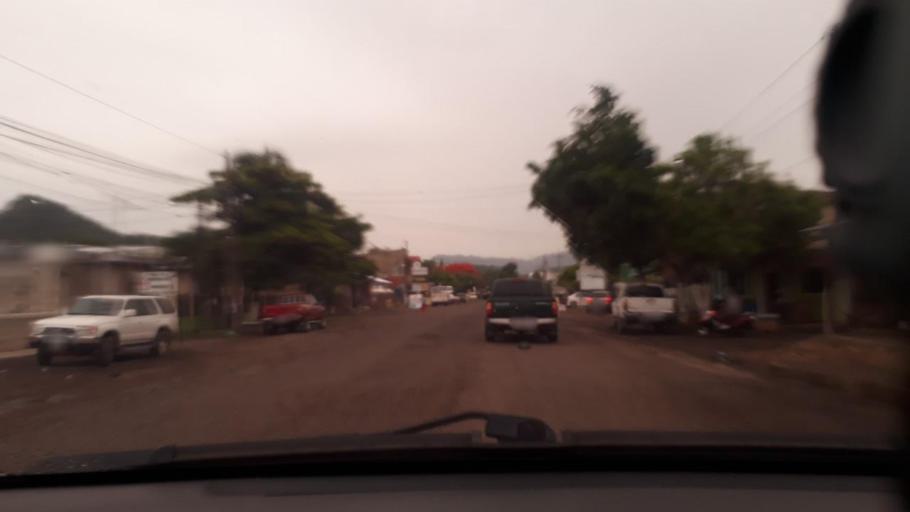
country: GT
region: Jutiapa
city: Asuncion Mita
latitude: 14.2891
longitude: -89.7218
